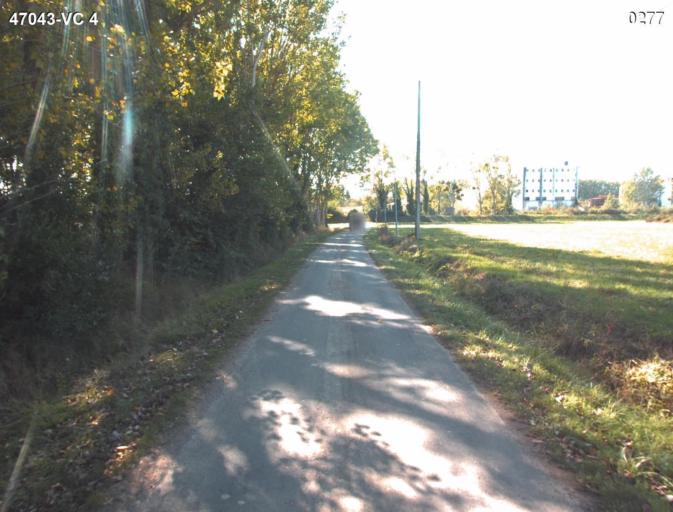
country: FR
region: Aquitaine
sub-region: Departement du Lot-et-Garonne
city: Buzet-sur-Baise
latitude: 44.2607
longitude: 0.3075
